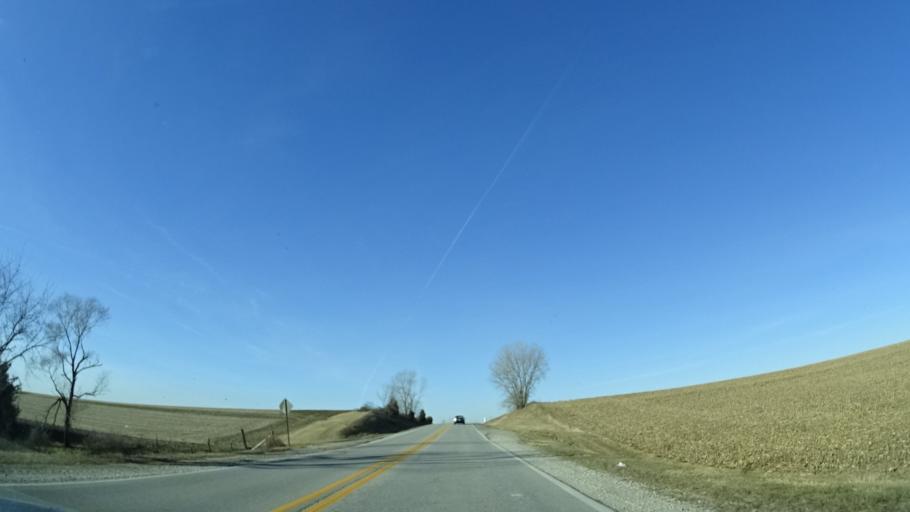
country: US
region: Nebraska
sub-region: Sarpy County
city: Springfield
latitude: 41.0889
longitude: -96.0834
